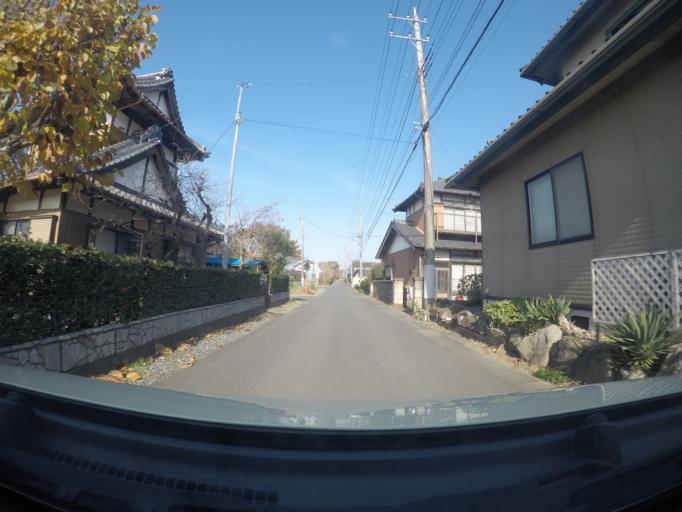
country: JP
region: Ibaraki
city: Tsukuba
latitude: 36.2271
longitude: 140.0653
